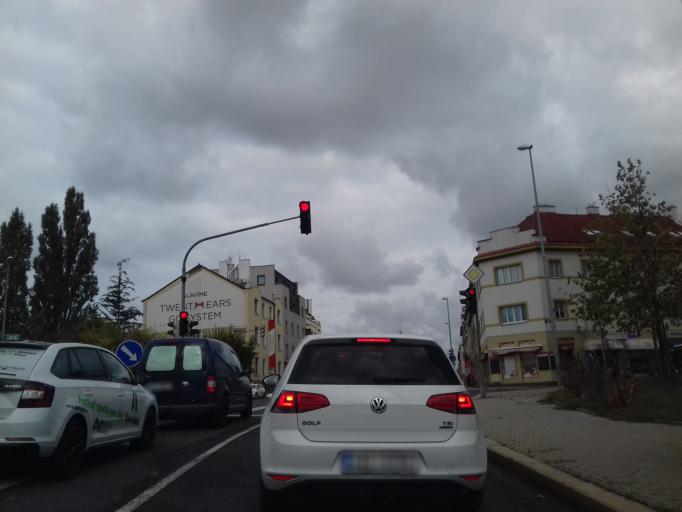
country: CZ
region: Praha
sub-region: Praha 4
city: Hodkovicky
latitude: 50.0401
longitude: 14.4384
